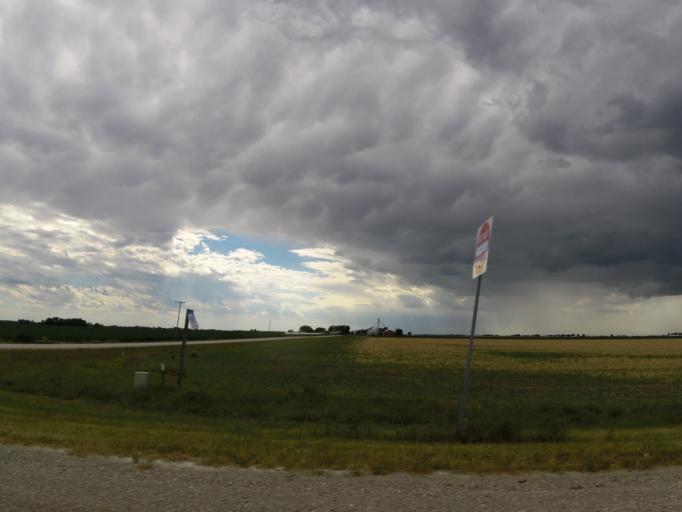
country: US
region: Iowa
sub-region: Henry County
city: Winfield
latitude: 41.0909
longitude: -91.5451
